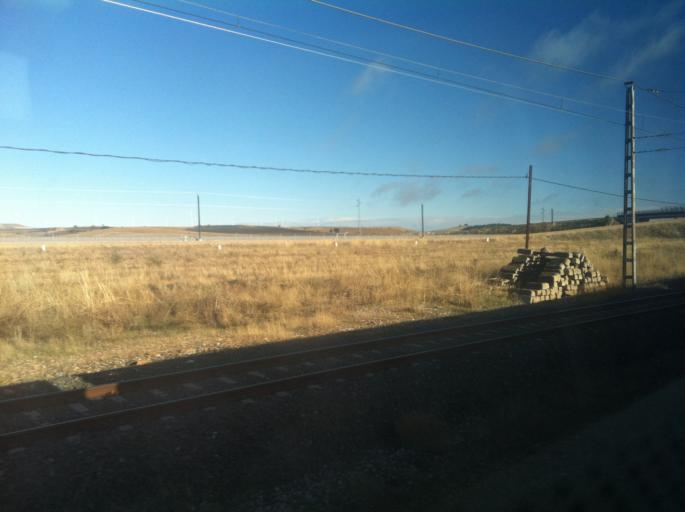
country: ES
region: Castille and Leon
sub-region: Provincia de Palencia
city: Villodrigo
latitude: 42.1478
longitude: -4.1050
